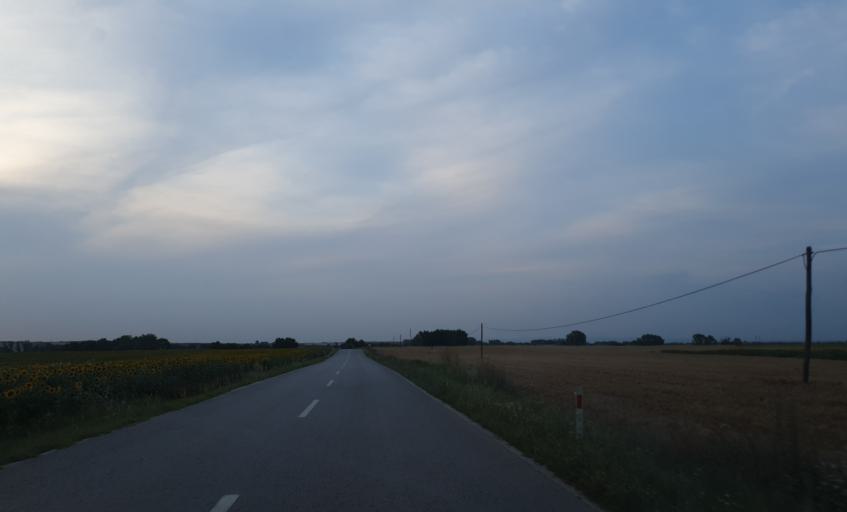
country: TR
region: Kirklareli
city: Buyukkaristiran
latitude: 41.3553
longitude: 27.6071
